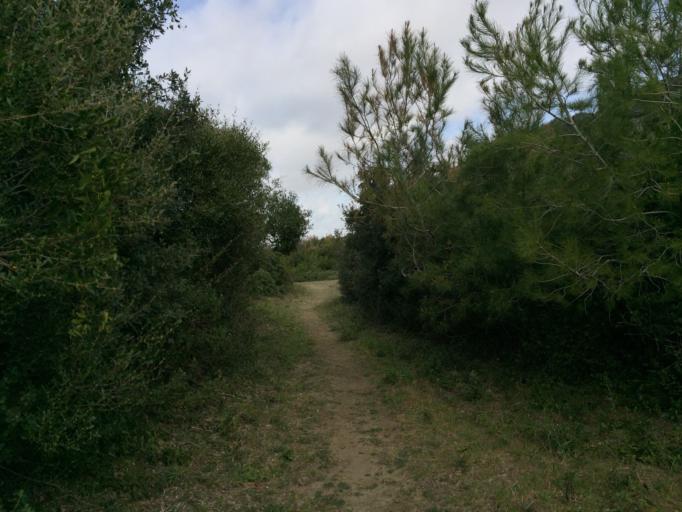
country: IT
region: Campania
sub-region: Provincia di Napoli
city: Monterusciello
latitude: 40.8481
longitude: 14.0482
